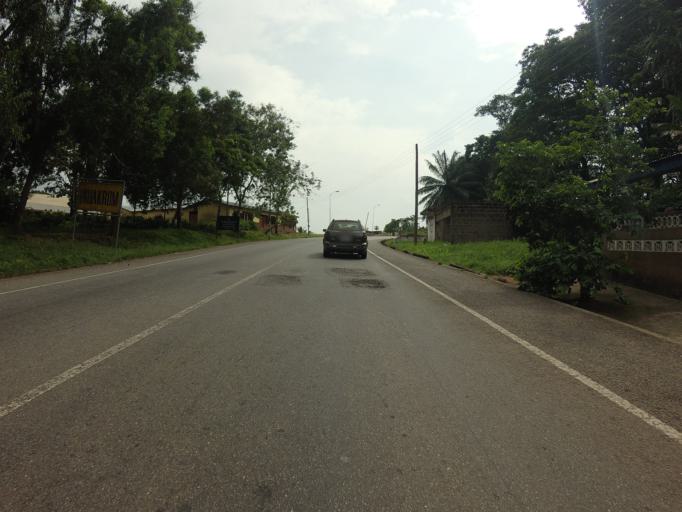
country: GH
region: Eastern
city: Aburi
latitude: 5.8428
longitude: -0.1742
